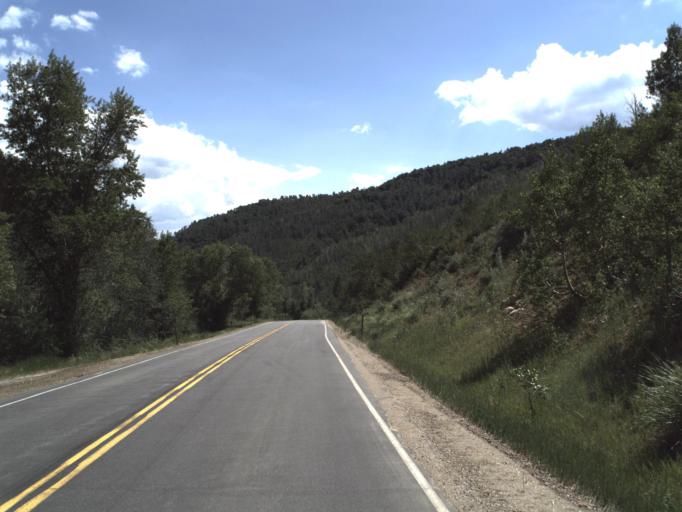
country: US
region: Utah
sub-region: Weber County
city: Wolf Creek
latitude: 41.4046
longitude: -111.5990
